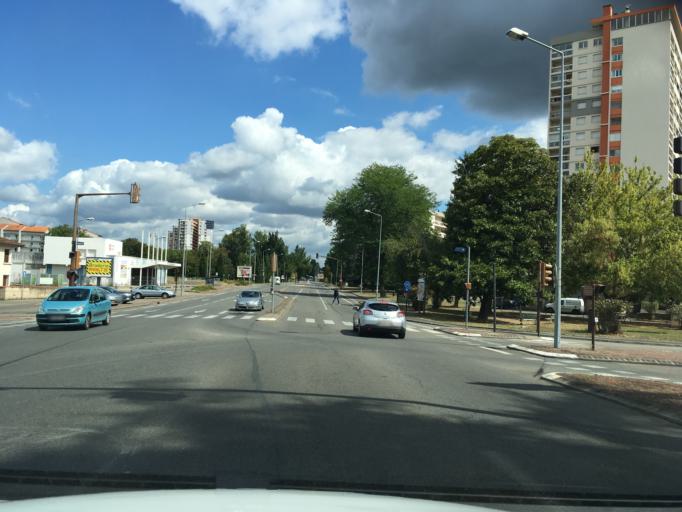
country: FR
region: Aquitaine
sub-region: Departement du Lot-et-Garonne
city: Agen
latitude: 44.2086
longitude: 0.6422
